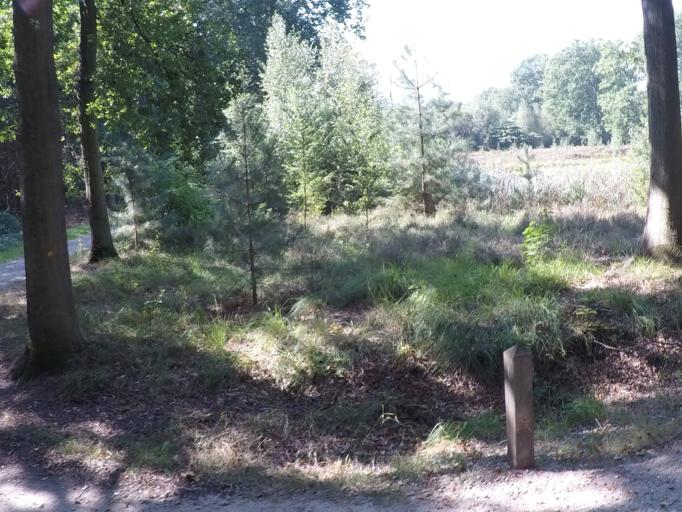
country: BE
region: Flanders
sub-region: Provincie Antwerpen
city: Kapellen
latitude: 51.3418
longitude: 4.4253
